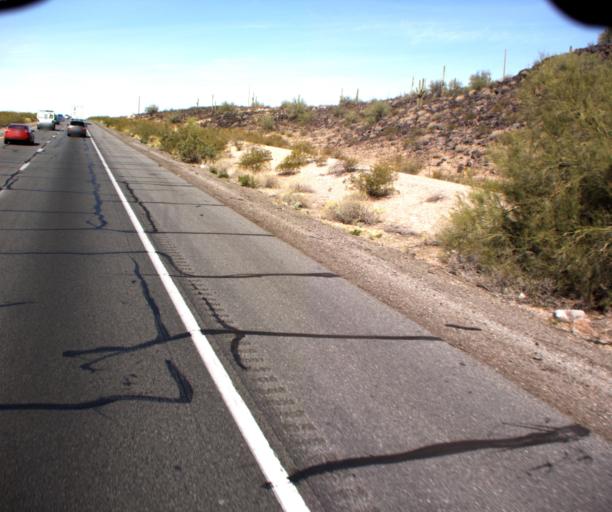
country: US
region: Arizona
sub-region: Maricopa County
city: Buckeye
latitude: 33.5290
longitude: -113.1159
